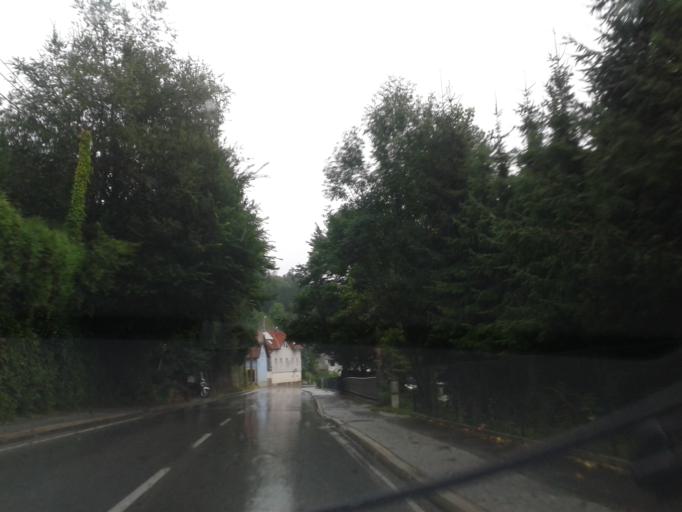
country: AT
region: Styria
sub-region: Graz Stadt
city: Goesting
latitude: 47.1018
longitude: 15.3856
